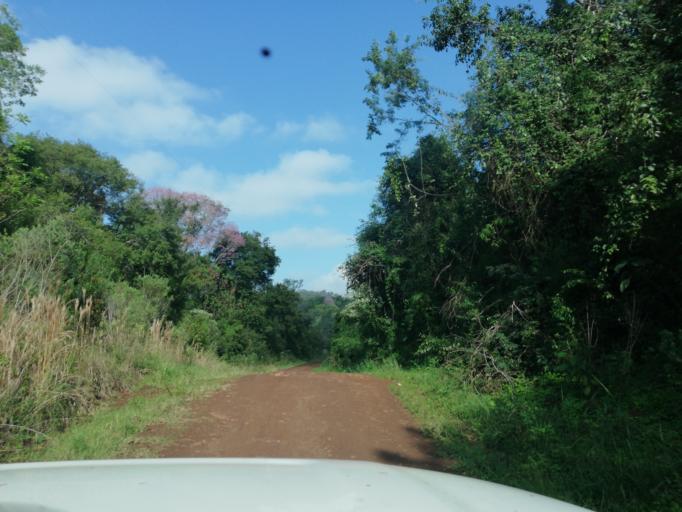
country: AR
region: Misiones
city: Cerro Azul
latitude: -27.6013
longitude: -55.5314
